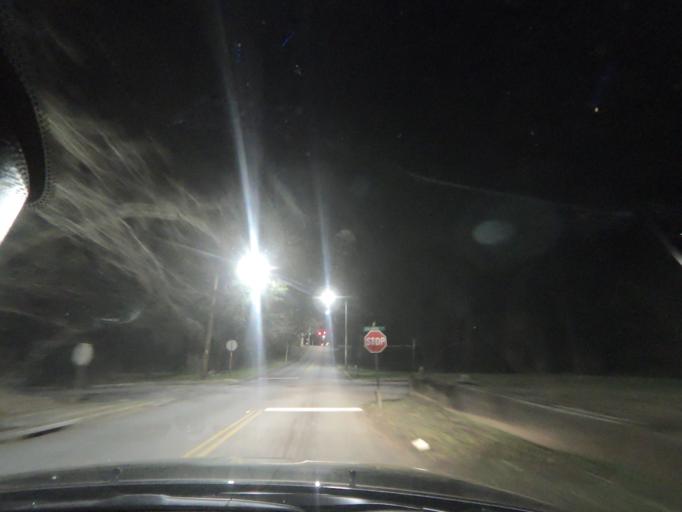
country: US
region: Georgia
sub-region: Fulton County
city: College Park
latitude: 33.6521
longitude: -84.4542
